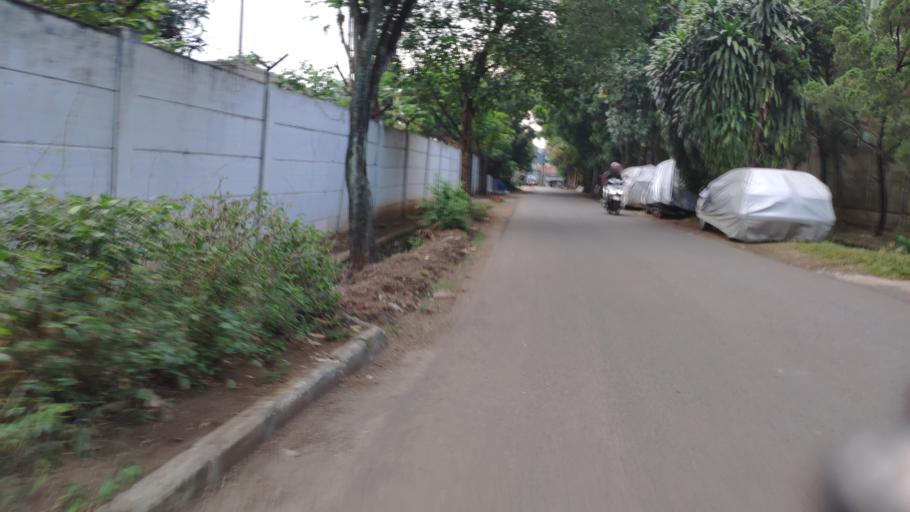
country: ID
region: West Java
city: Pamulang
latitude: -6.2981
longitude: 106.8097
